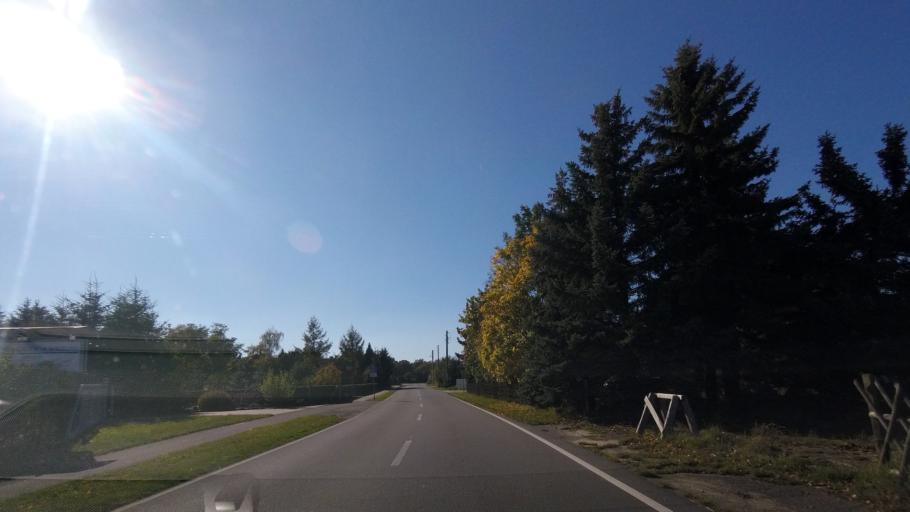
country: DE
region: Saxony-Anhalt
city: Muhlanger
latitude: 51.8593
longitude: 12.7760
